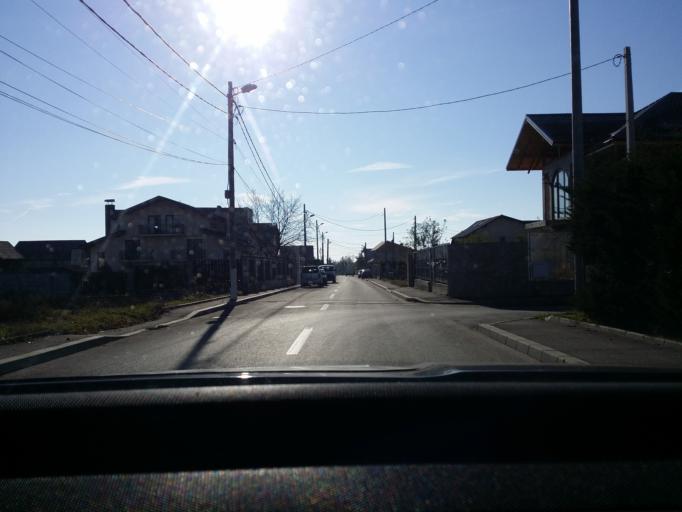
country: RO
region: Prahova
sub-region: Municipiul Campina
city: Campina
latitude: 45.1426
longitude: 25.7278
